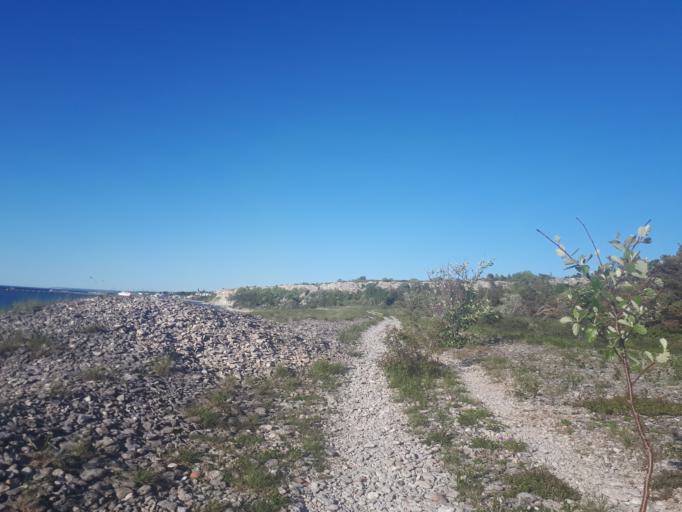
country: SE
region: Gotland
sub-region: Gotland
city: Vibble
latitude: 57.6154
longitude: 18.2539
